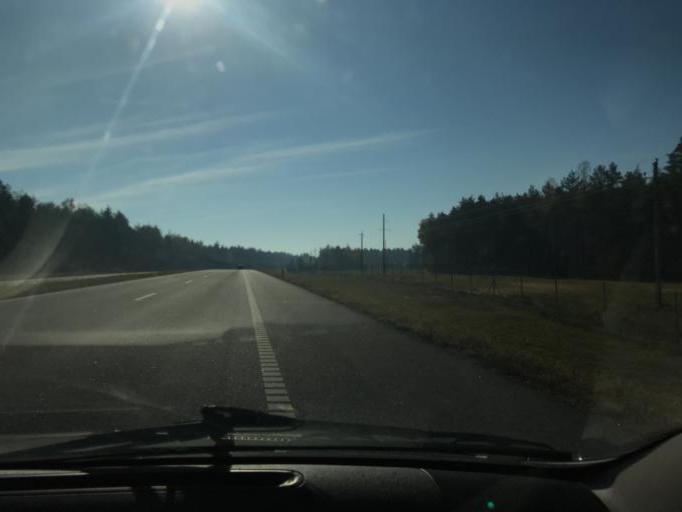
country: BY
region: Minsk
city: Slutsk
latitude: 53.2900
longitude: 27.5481
